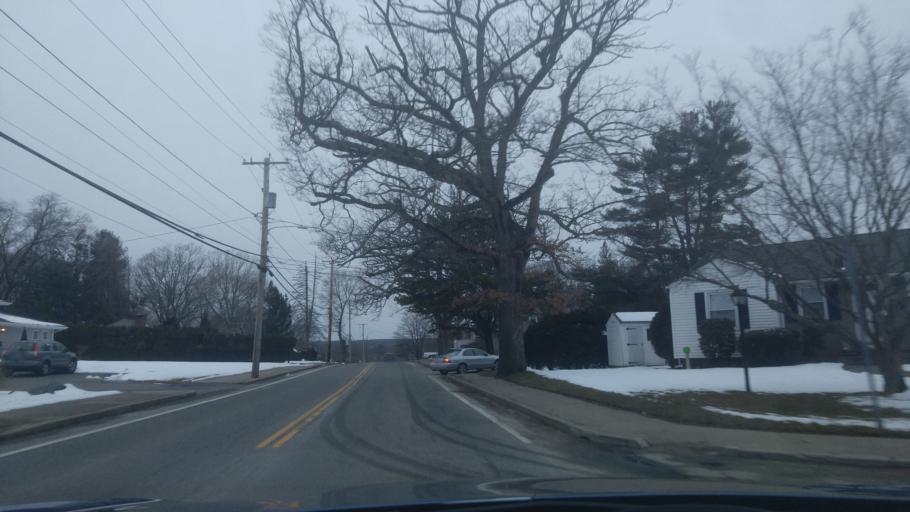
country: US
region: Rhode Island
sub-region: Providence County
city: Cranston
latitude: 41.7343
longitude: -71.4739
